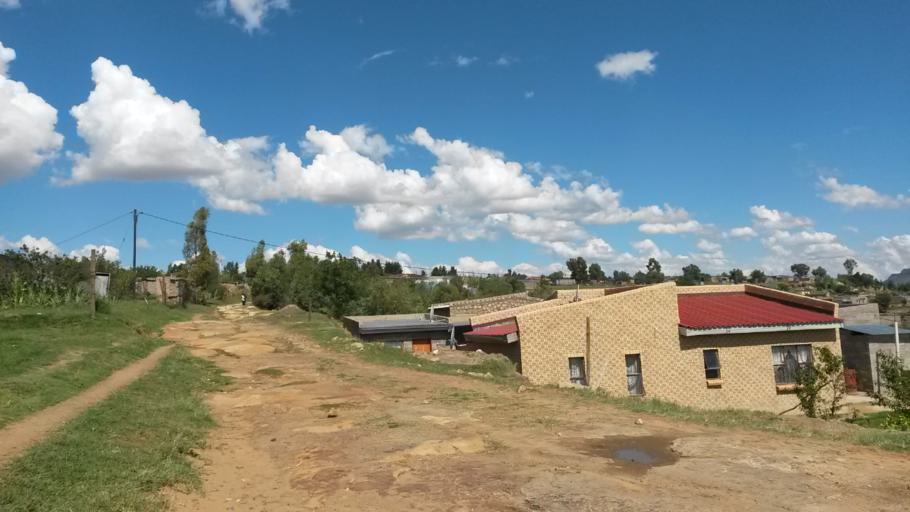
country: LS
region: Maseru
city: Maseru
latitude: -29.3677
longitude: 27.5026
